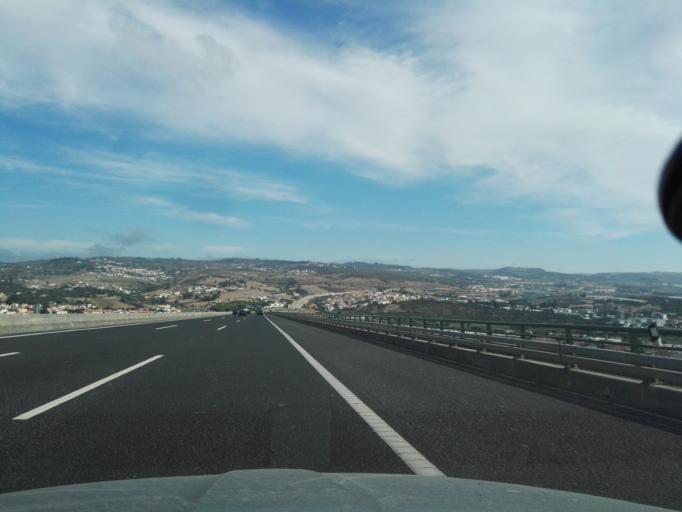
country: PT
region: Lisbon
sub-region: Loures
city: Loures
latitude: 38.8298
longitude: -9.1906
